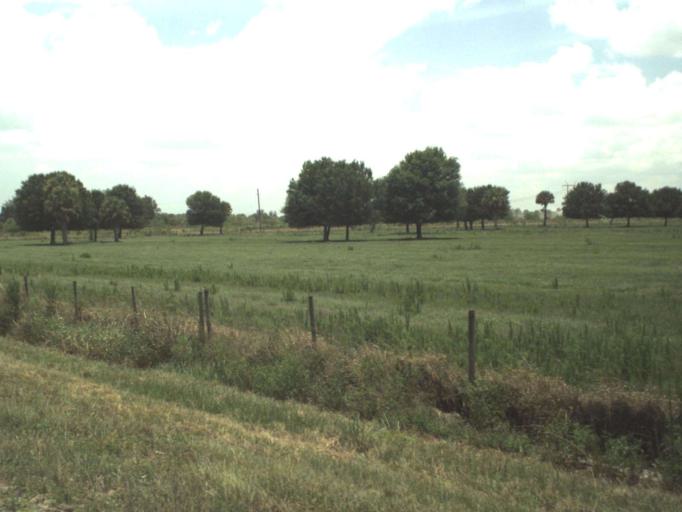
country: US
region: Florida
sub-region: Saint Lucie County
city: Fort Pierce South
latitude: 27.3745
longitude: -80.4768
